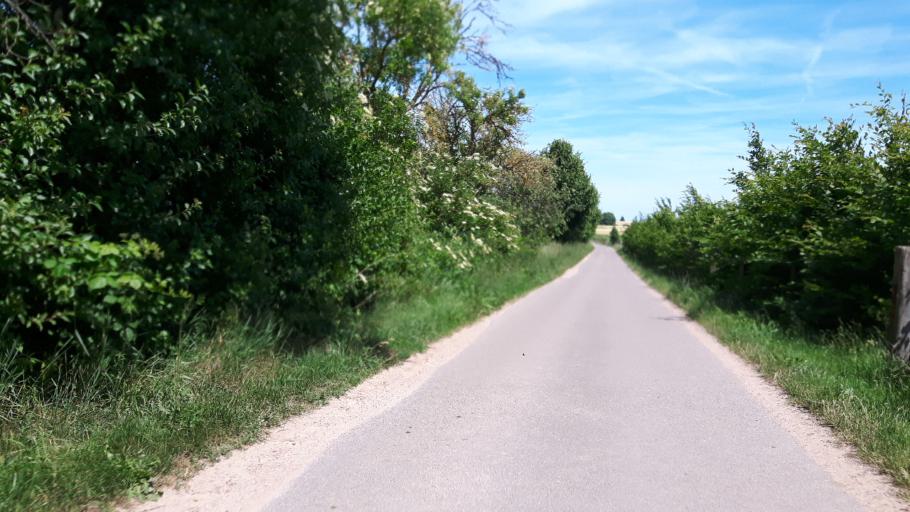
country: DE
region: Saxony-Anhalt
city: Kropstadt
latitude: 52.0016
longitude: 12.7149
